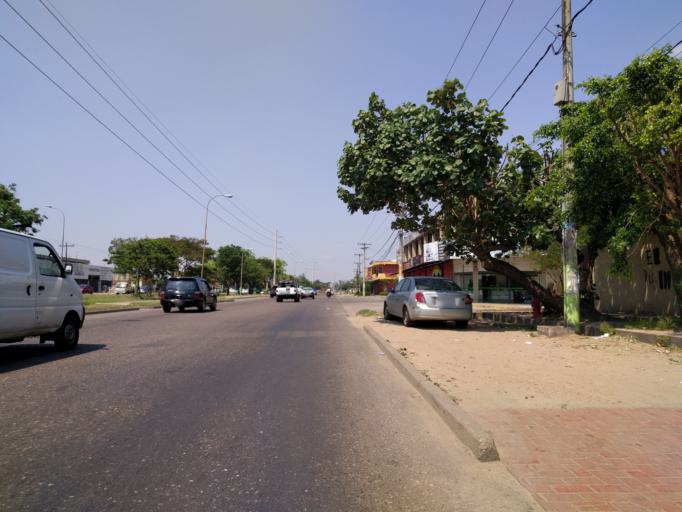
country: BO
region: Santa Cruz
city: Santa Cruz de la Sierra
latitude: -17.7994
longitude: -63.1506
